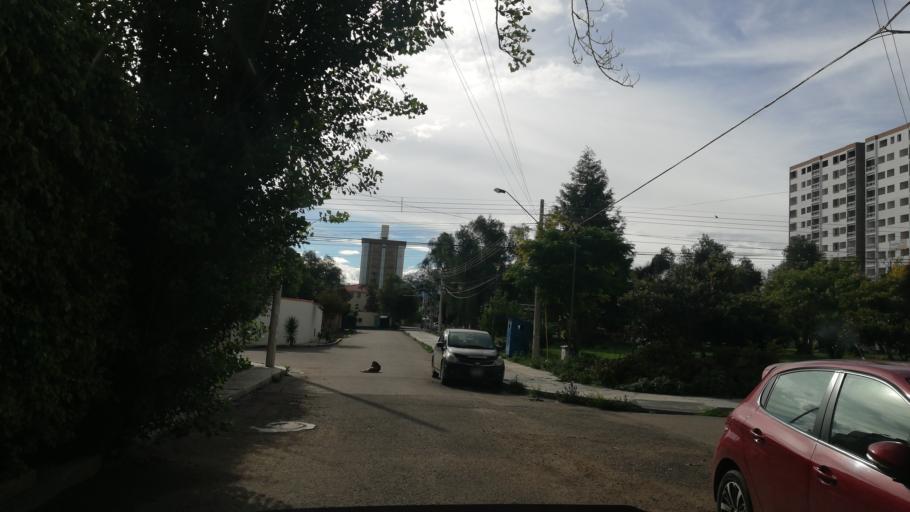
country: BO
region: Cochabamba
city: Cochabamba
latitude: -17.3740
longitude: -66.1775
